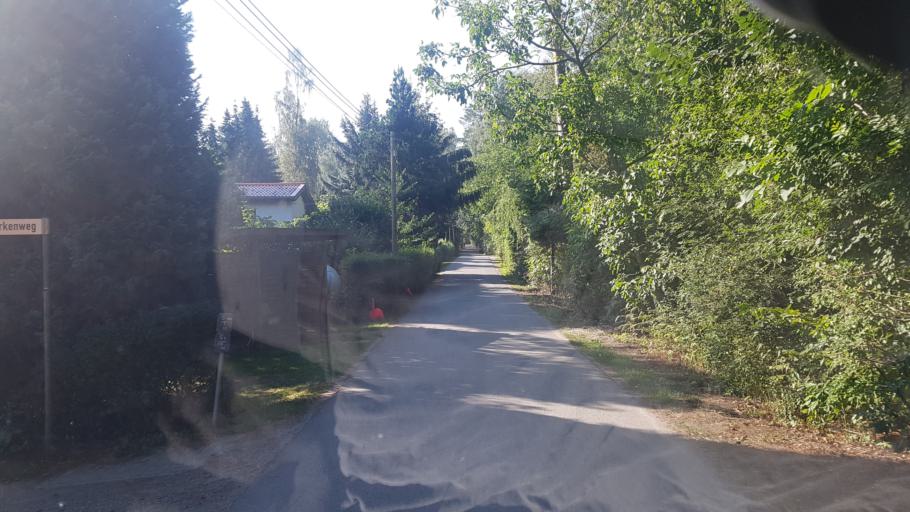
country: DE
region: Brandenburg
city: Plessa
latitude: 51.5177
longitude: 13.6509
